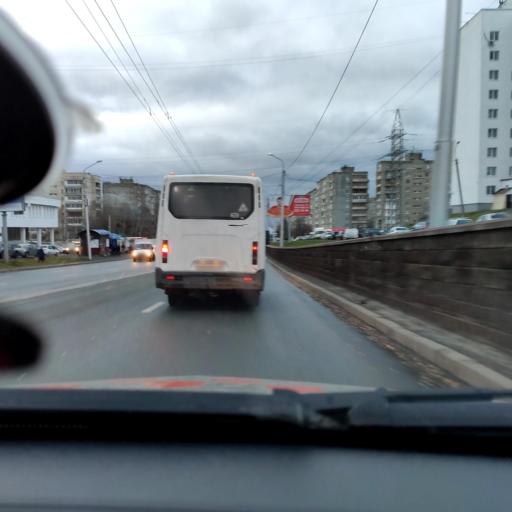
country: RU
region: Bashkortostan
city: Ufa
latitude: 54.7048
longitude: 55.9969
